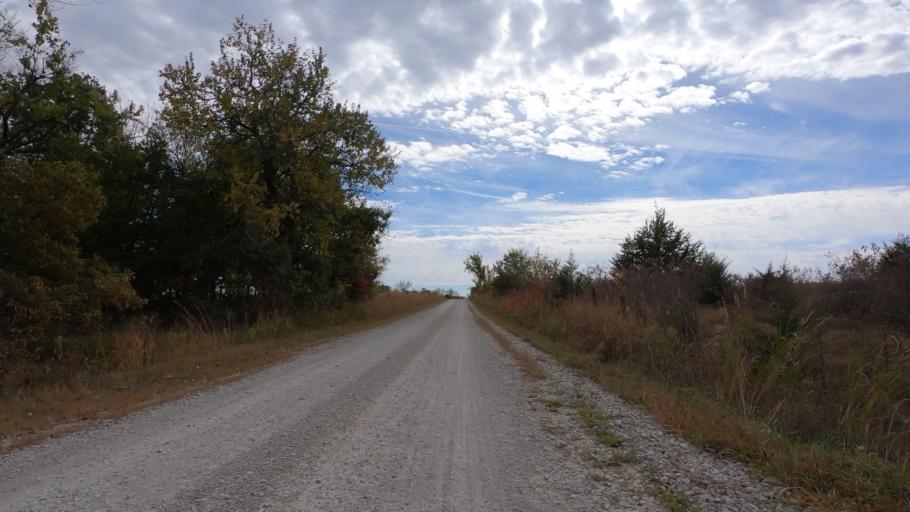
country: US
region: Kansas
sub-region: Pottawatomie County
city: Westmoreland
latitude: 39.3454
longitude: -96.4453
